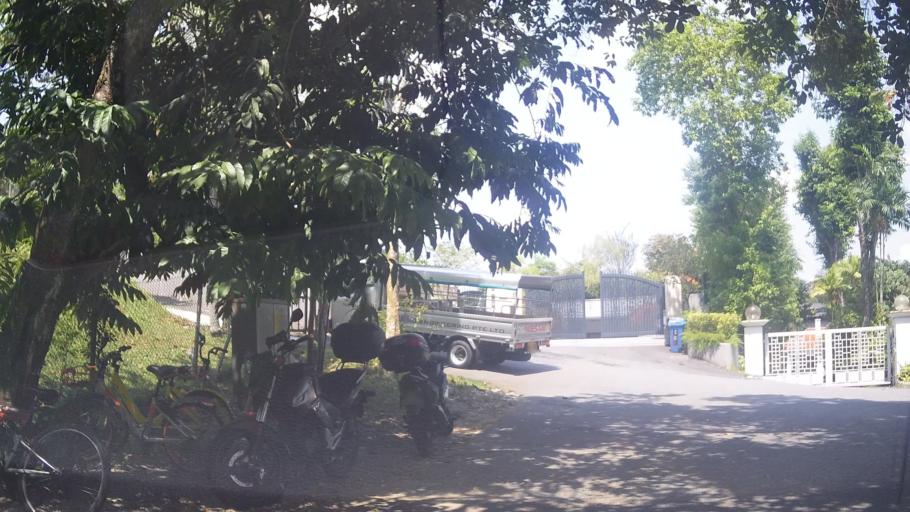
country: SG
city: Singapore
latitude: 1.3203
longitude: 103.8027
